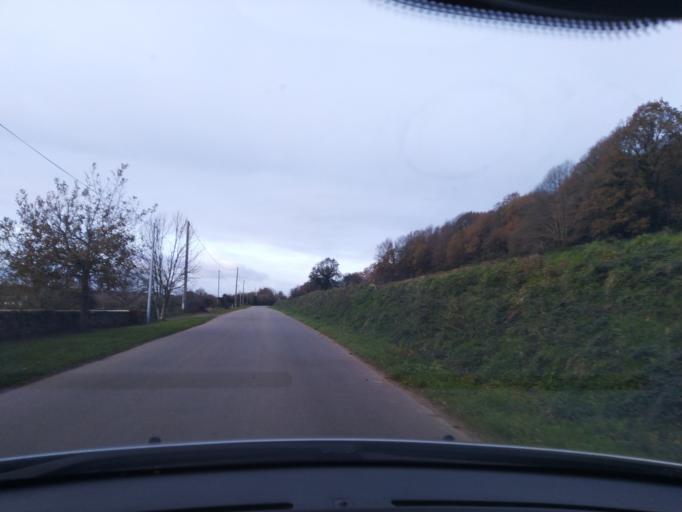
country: FR
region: Brittany
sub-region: Departement du Finistere
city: Guerlesquin
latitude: 48.5409
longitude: -3.6179
